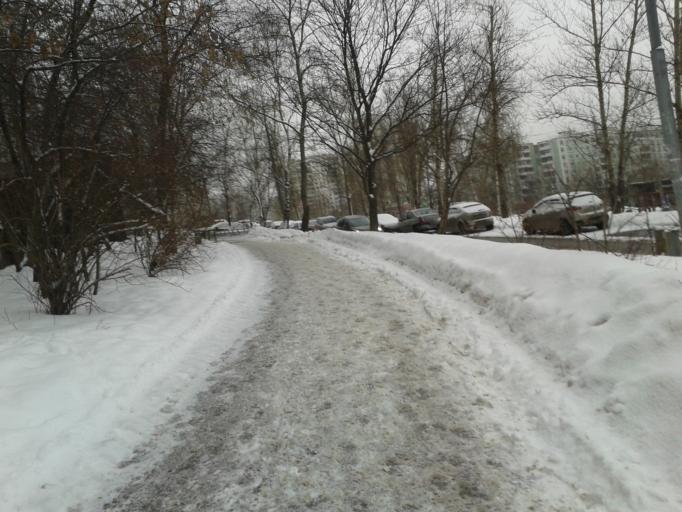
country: RU
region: Moscow
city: Strogino
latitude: 55.8057
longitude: 37.4090
